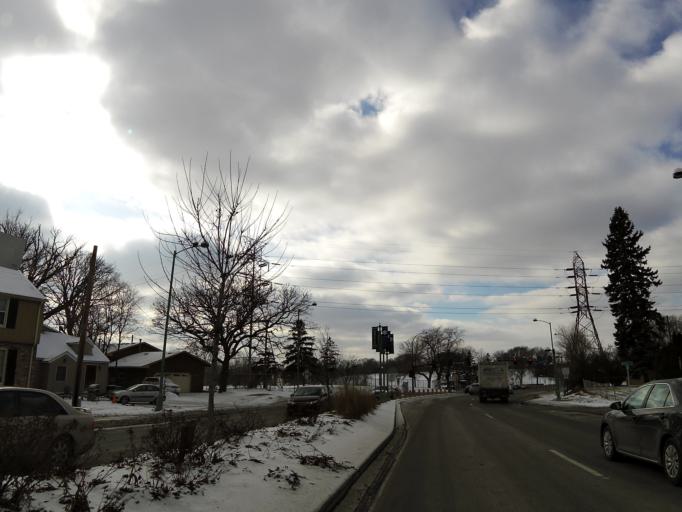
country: US
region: Minnesota
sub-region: Hennepin County
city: Saint Louis Park
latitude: 44.9273
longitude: -93.3599
